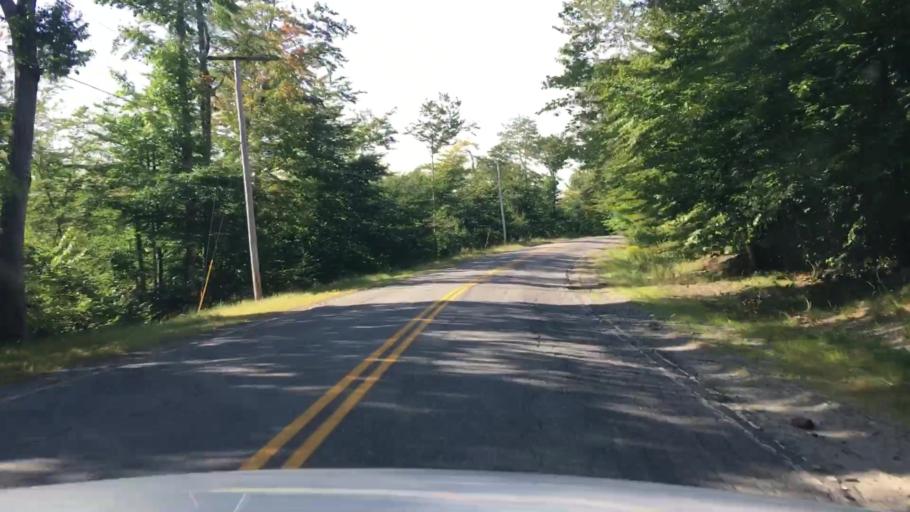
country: US
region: Maine
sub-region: Penobscot County
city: Enfield
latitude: 45.2258
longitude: -68.5408
